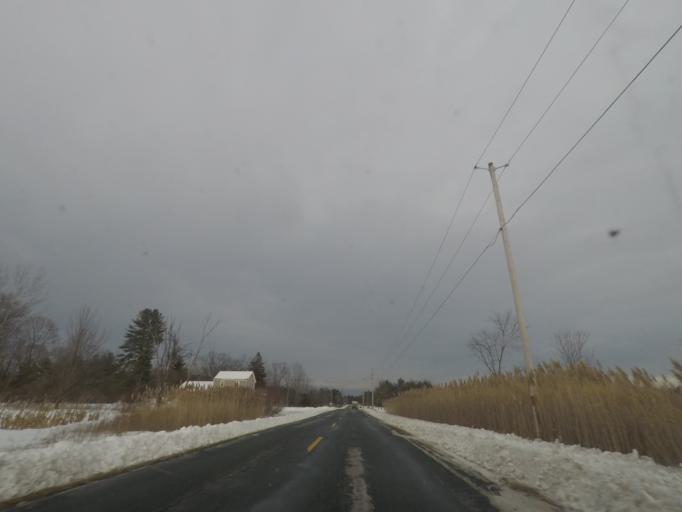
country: US
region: New York
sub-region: Rensselaer County
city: Castleton-on-Hudson
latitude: 42.5171
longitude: -73.7395
